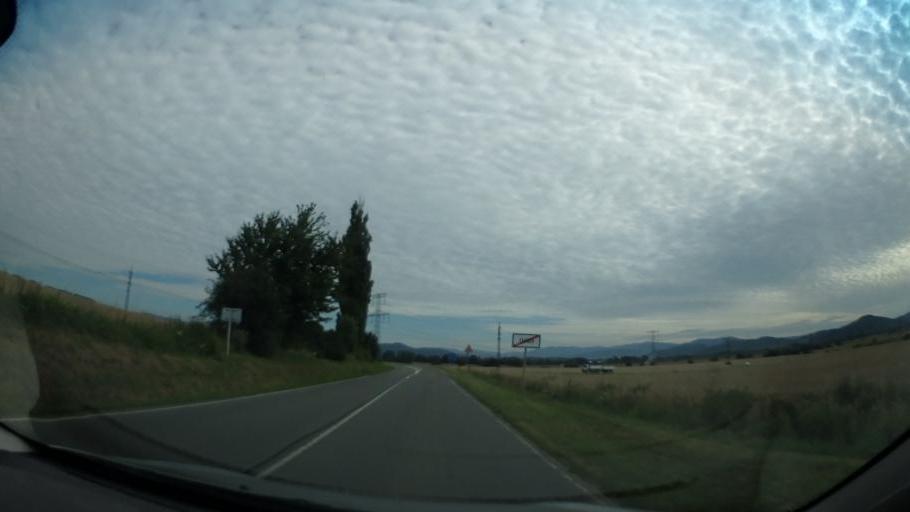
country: CZ
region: Olomoucky
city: Zabreh
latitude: 49.8917
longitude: 16.8802
